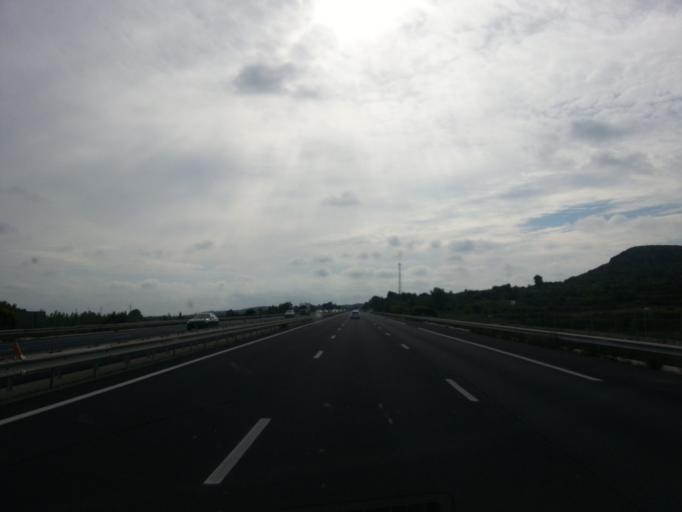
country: FR
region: Languedoc-Roussillon
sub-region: Departement du Gard
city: Sernhac
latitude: 43.9031
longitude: 4.5428
